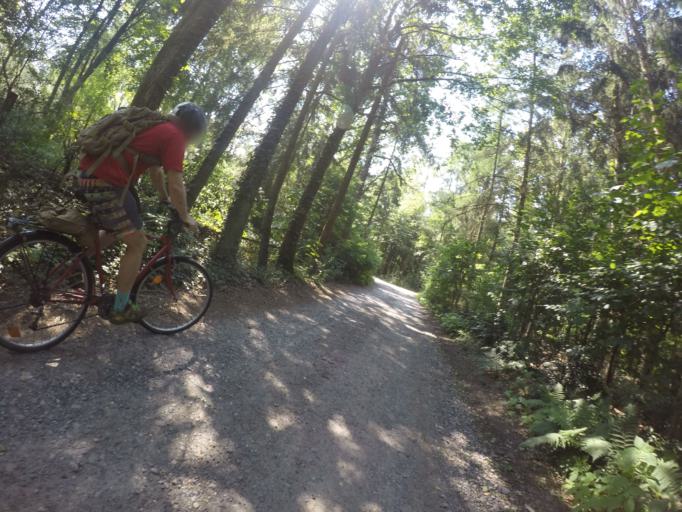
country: DE
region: Lower Saxony
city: Buchholz in der Nordheide
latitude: 53.3070
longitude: 9.8190
